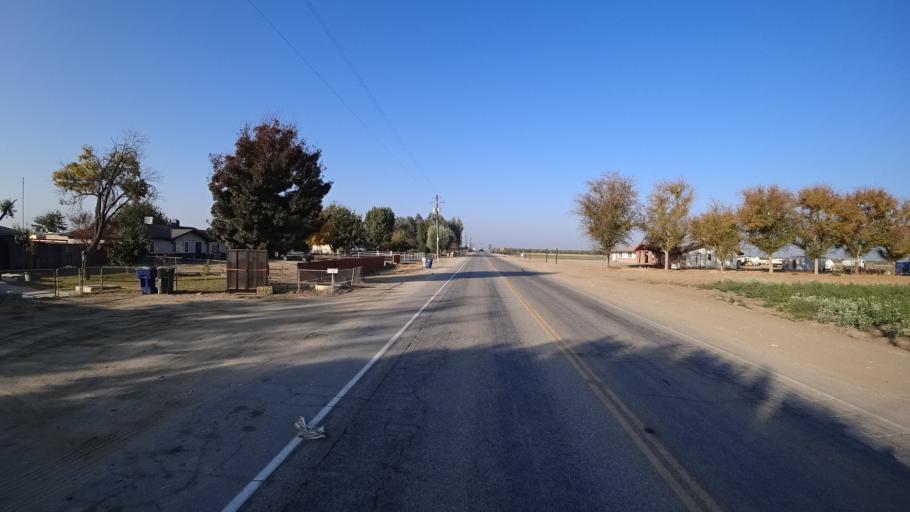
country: US
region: California
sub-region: Kern County
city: Greenfield
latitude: 35.2523
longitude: -118.9818
